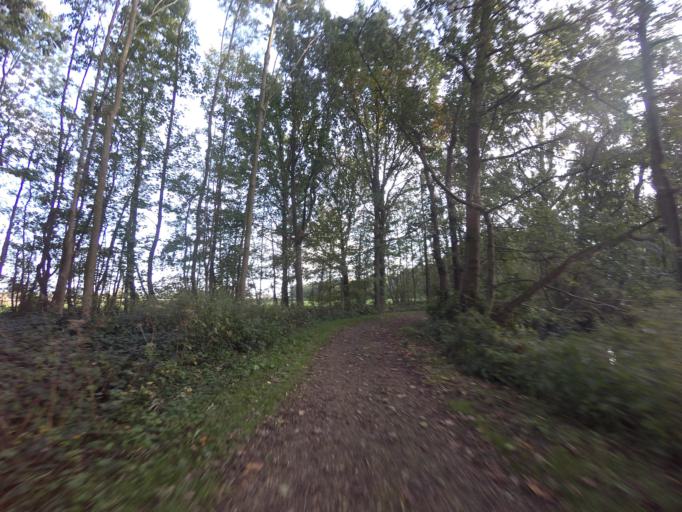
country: BE
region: Flanders
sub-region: Provincie Antwerpen
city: Rumst
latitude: 51.0586
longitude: 4.4054
